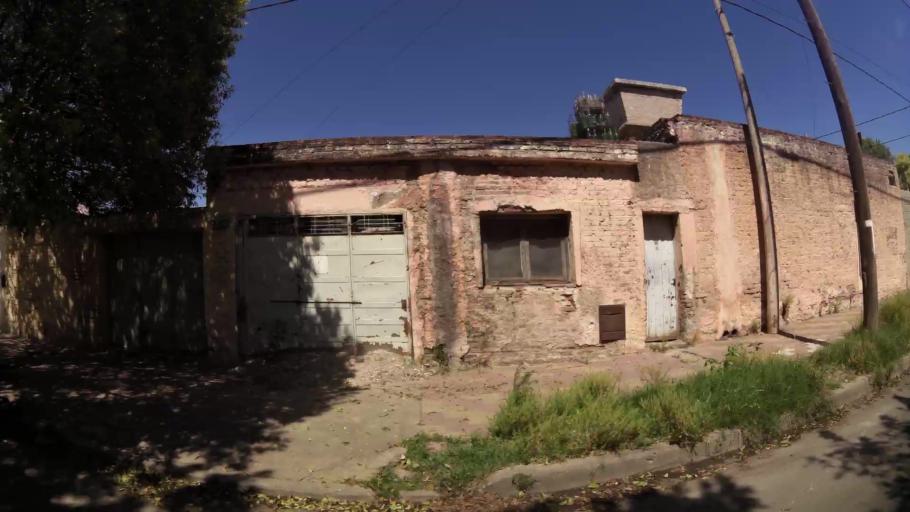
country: AR
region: Cordoba
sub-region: Departamento de Capital
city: Cordoba
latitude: -31.3707
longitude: -64.1430
